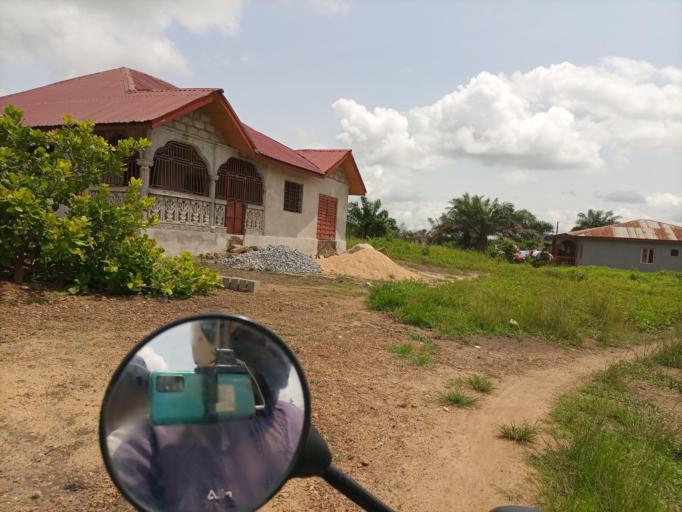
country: SL
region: Southern Province
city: Bo
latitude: 7.9786
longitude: -11.7694
